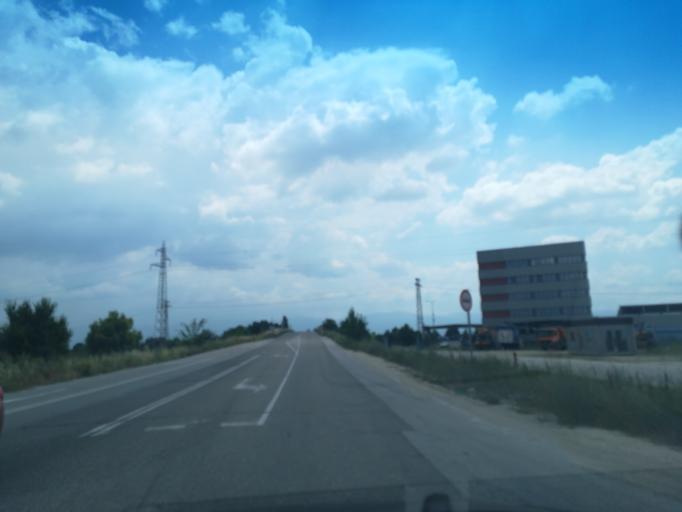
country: BG
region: Plovdiv
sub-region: Obshtina Plovdiv
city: Plovdiv
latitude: 42.1929
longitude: 24.6765
